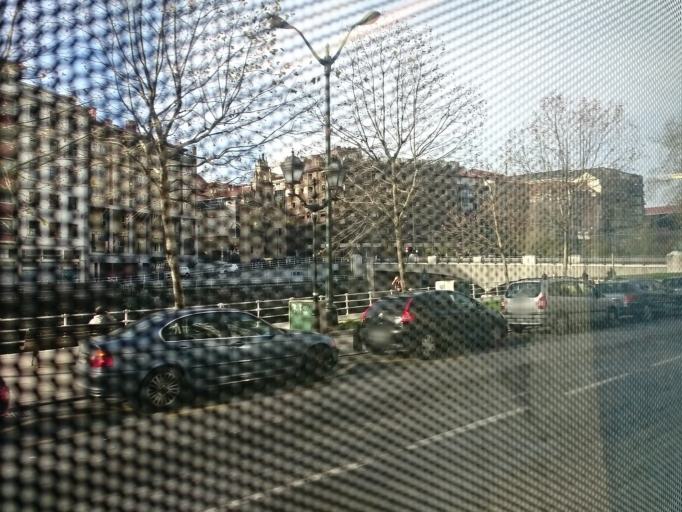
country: ES
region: Basque Country
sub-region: Bizkaia
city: Bilbao
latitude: 43.2571
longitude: -2.9262
